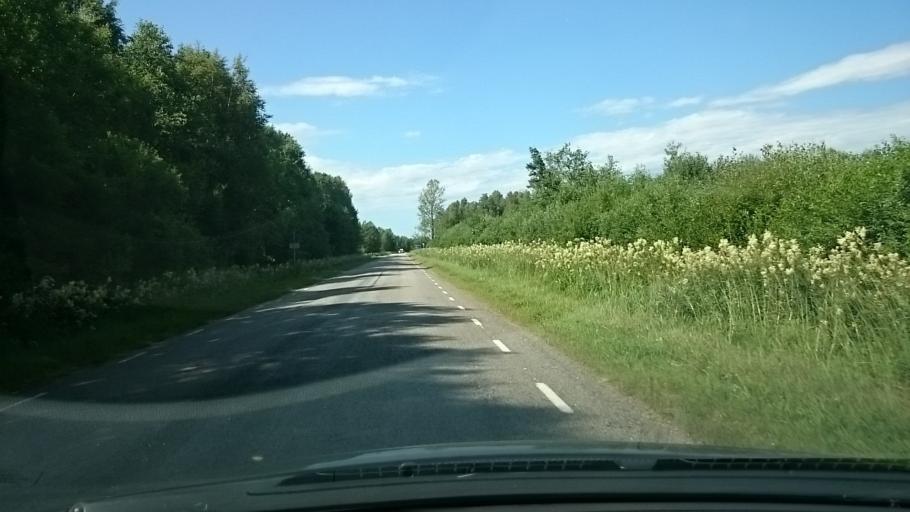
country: EE
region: Laeaene
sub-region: Haapsalu linn
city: Haapsalu
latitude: 59.0868
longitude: 23.5516
